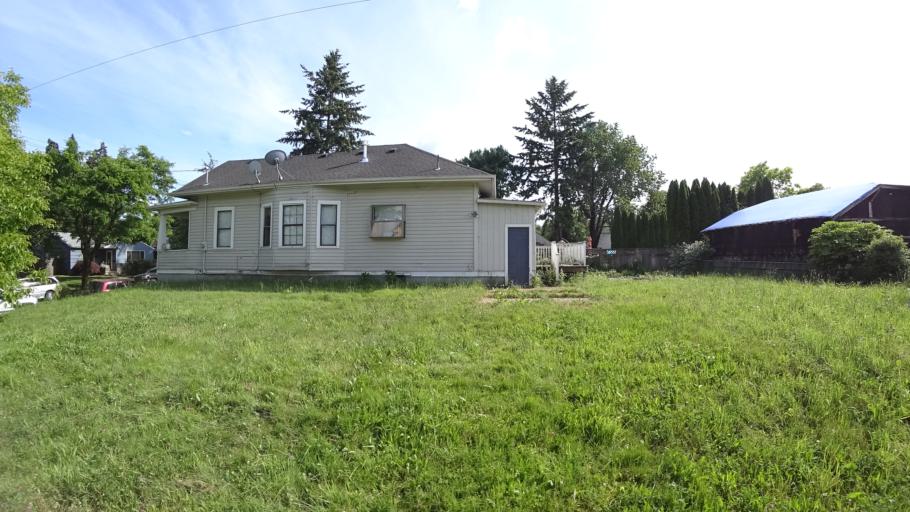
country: US
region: Oregon
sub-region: Washington County
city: West Haven
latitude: 45.5948
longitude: -122.7470
